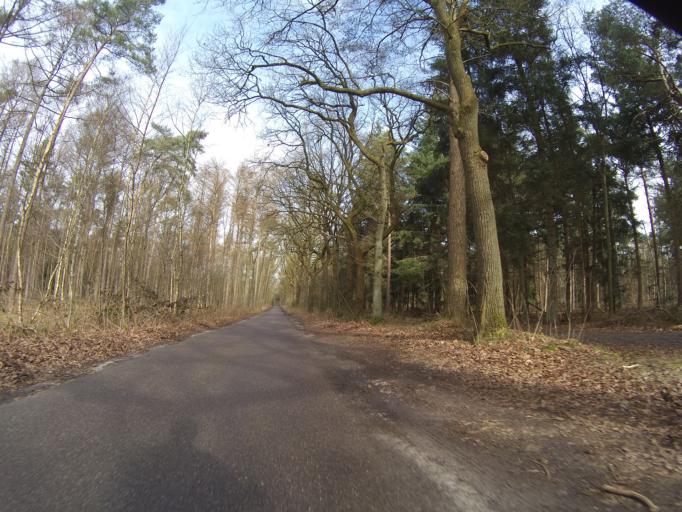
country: NL
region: Utrecht
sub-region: Gemeente Amersfoort
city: Hoogland
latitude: 52.1514
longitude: 5.3373
